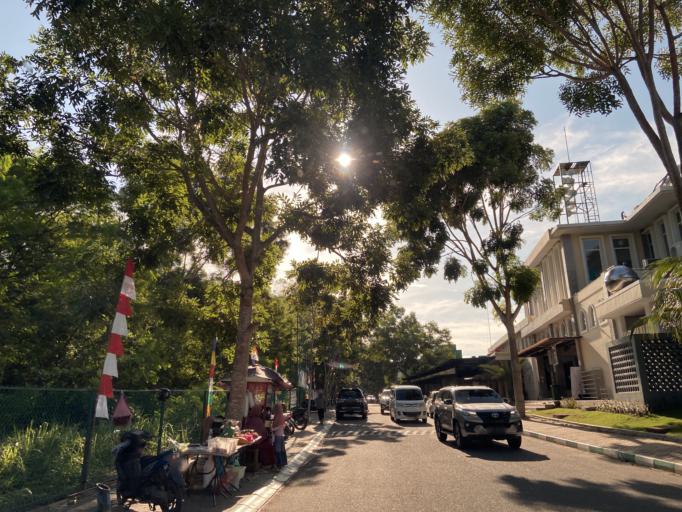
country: SG
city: Singapore
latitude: 1.1051
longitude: 104.0310
